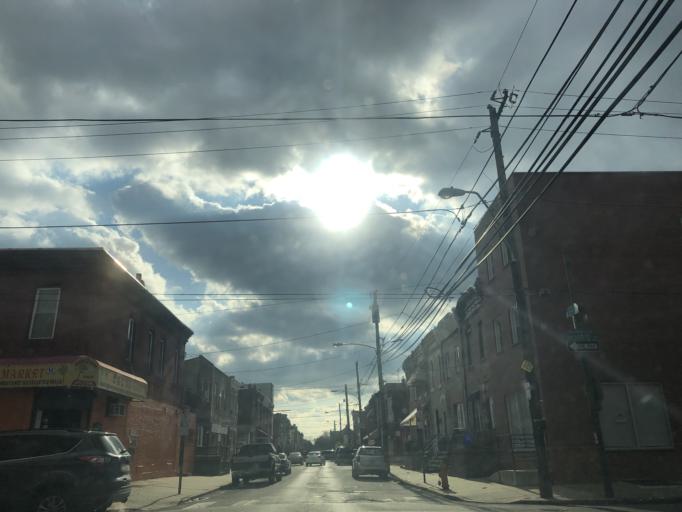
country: US
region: Pennsylvania
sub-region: Philadelphia County
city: Philadelphia
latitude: 39.9309
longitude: -75.1801
